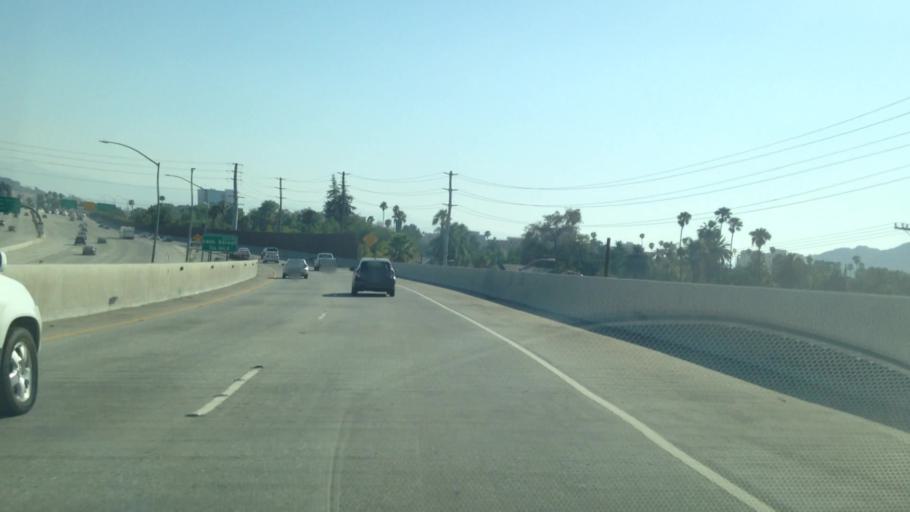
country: US
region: California
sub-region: Riverside County
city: Highgrove
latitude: 33.9886
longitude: -117.3632
